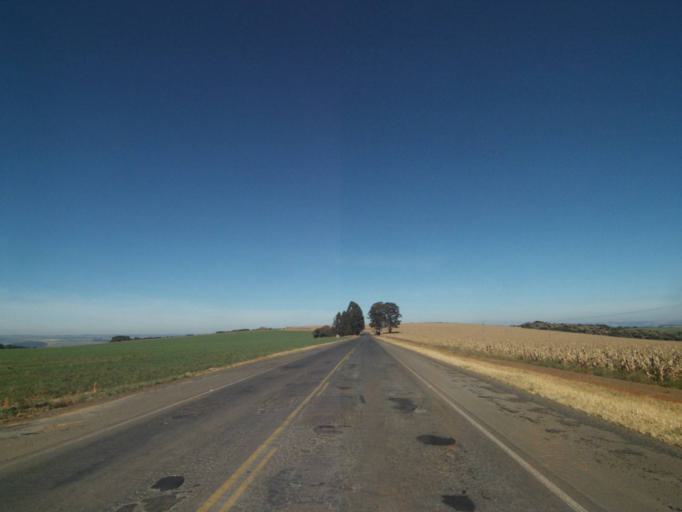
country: BR
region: Parana
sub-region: Tibagi
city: Tibagi
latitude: -24.3862
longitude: -50.3337
